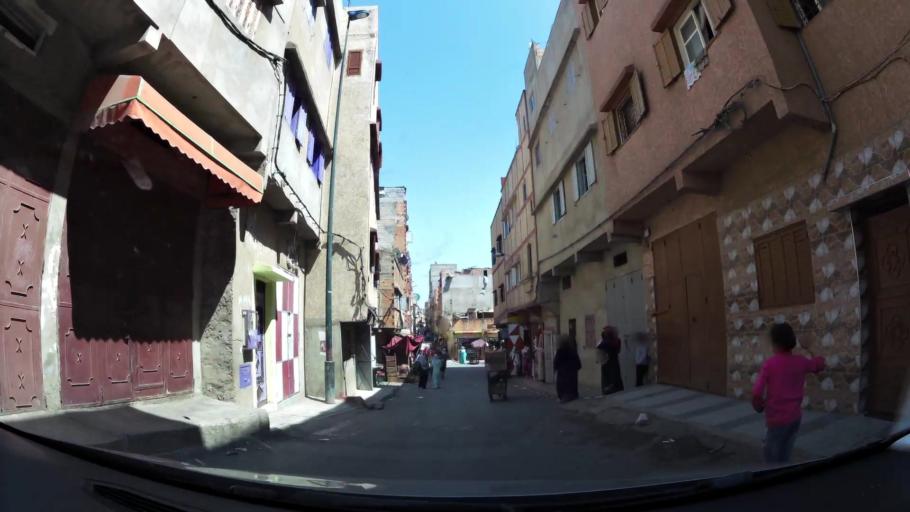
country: MA
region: Rabat-Sale-Zemmour-Zaer
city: Sale
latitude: 34.0660
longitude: -6.7772
